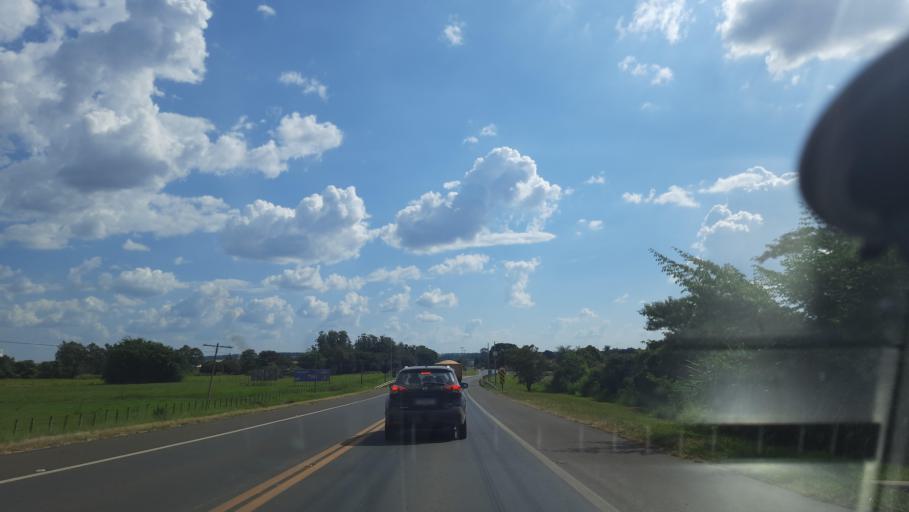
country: BR
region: Sao Paulo
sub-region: Casa Branca
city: Casa Branca
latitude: -21.7404
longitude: -46.9777
